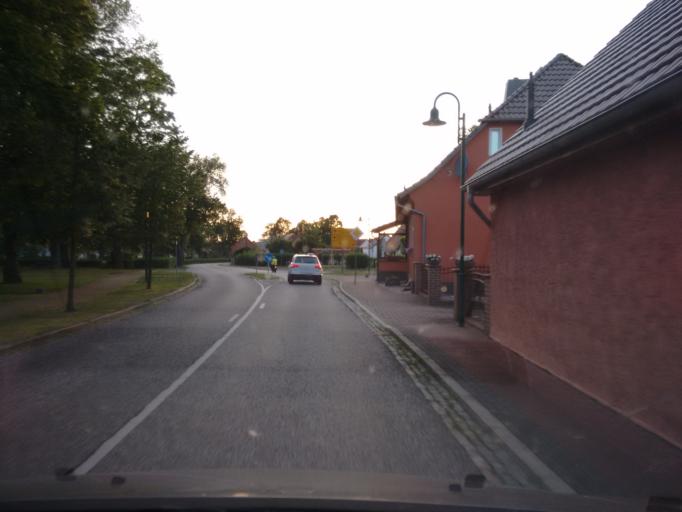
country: DE
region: Brandenburg
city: Mixdorf
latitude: 52.1577
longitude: 14.3951
